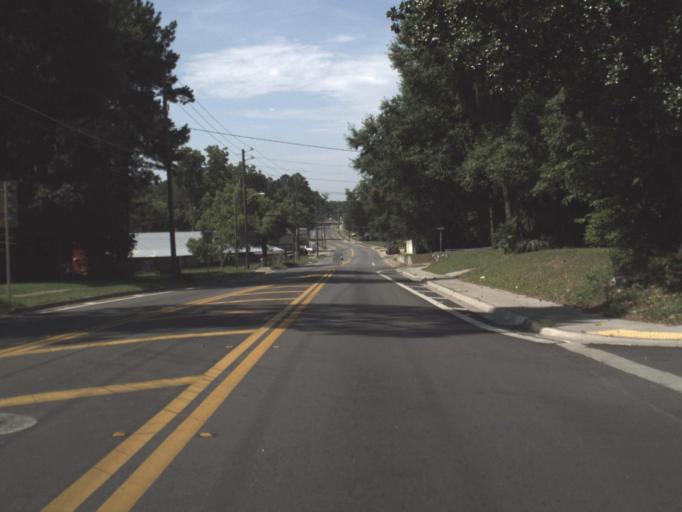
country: US
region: Florida
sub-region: Madison County
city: Madison
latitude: 30.4686
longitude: -83.4101
